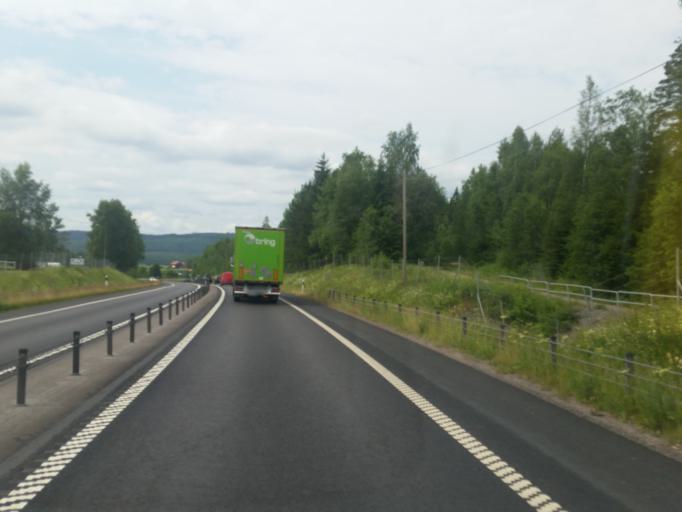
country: SE
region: Dalarna
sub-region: Borlange Kommun
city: Borlaenge
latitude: 60.4372
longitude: 15.3530
